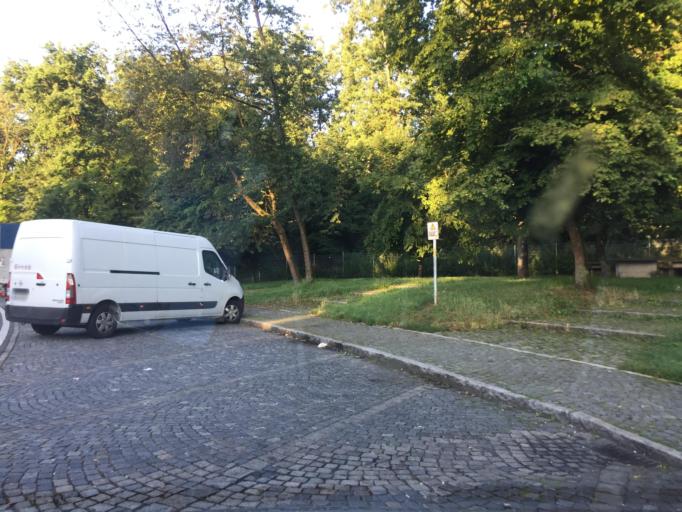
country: DE
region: Bavaria
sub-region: Regierungsbezirk Mittelfranken
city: Schwaig
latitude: 49.4226
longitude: 11.2053
